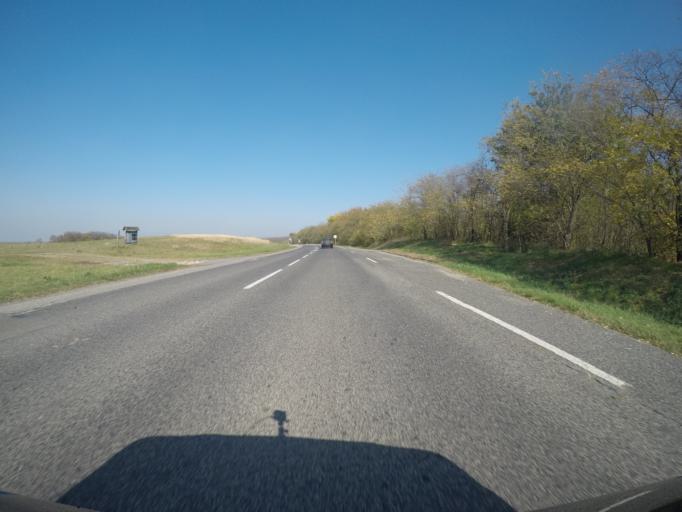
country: HU
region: Tolna
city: Szedres
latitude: 46.4606
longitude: 18.6884
